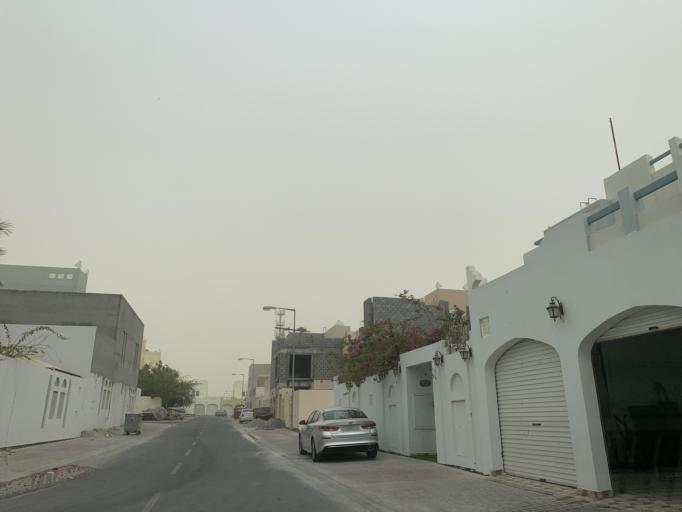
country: BH
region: Central Governorate
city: Madinat Hamad
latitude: 26.1302
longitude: 50.5098
